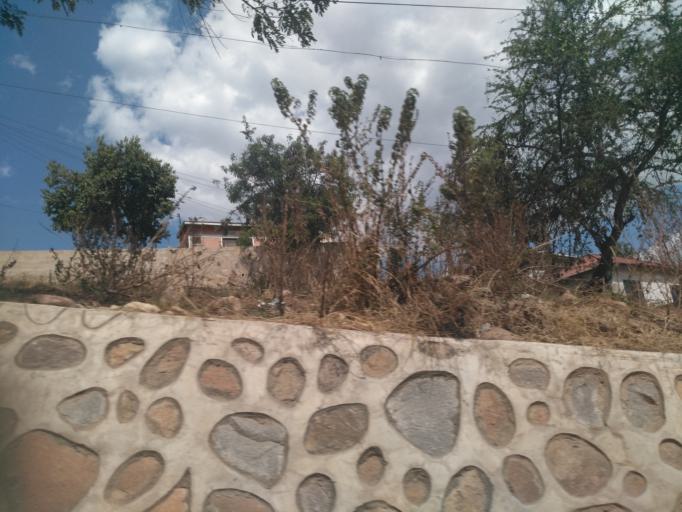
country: TZ
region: Mwanza
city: Mwanza
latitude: -2.5020
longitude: 32.9119
